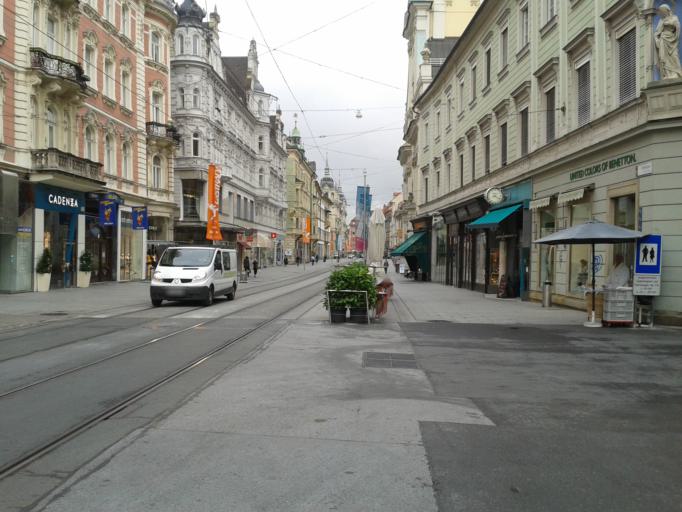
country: AT
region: Styria
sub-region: Graz Stadt
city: Graz
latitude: 47.0686
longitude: 15.4414
